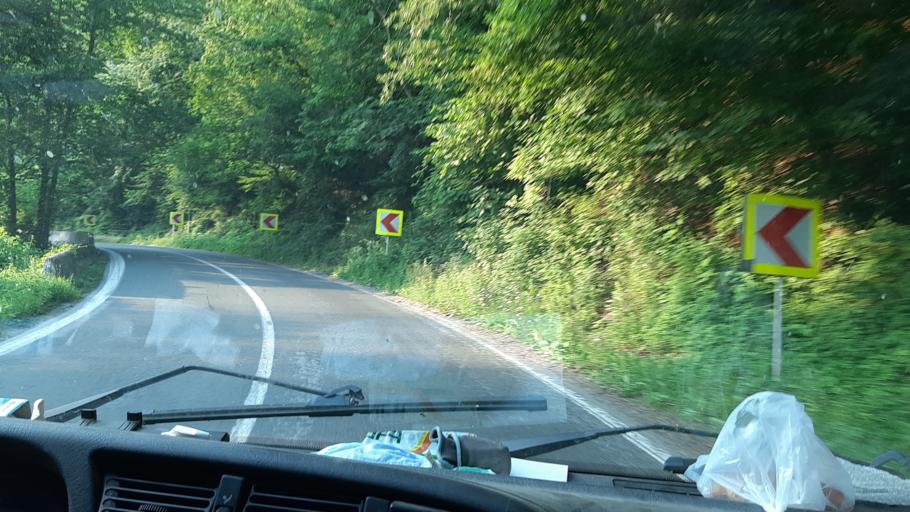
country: RO
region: Caras-Severin
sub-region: Municipiul Resita
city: Calnic
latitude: 45.3607
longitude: 21.8225
